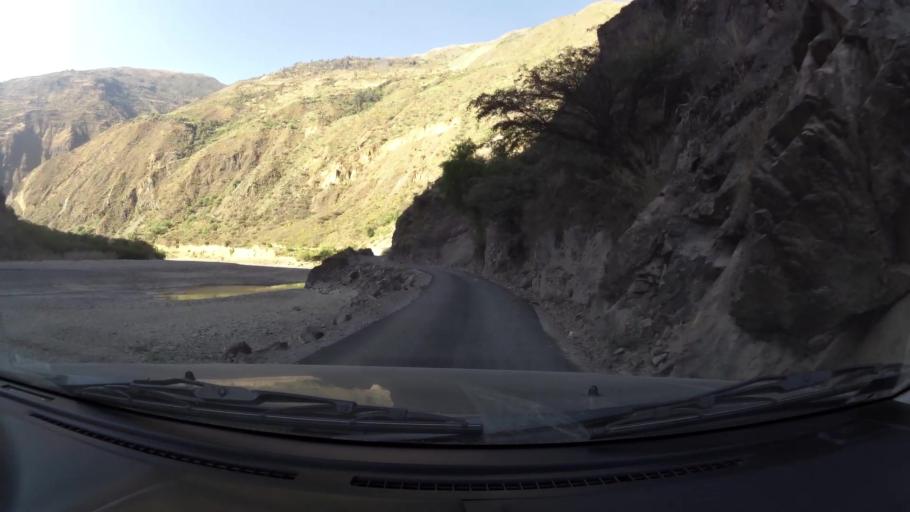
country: PE
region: Huancavelica
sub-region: Provincia de Churcampa
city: La Esmeralda
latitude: -12.5767
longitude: -74.6914
